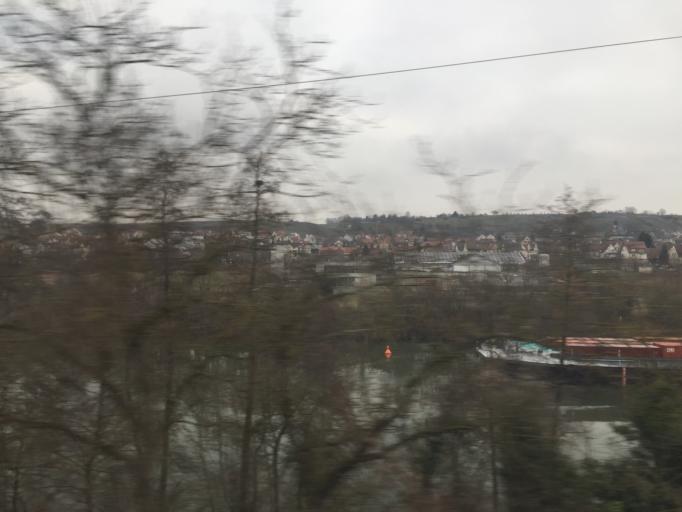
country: DE
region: Baden-Wuerttemberg
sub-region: Regierungsbezirk Stuttgart
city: Gemmrigheim
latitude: 49.0306
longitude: 9.1502
